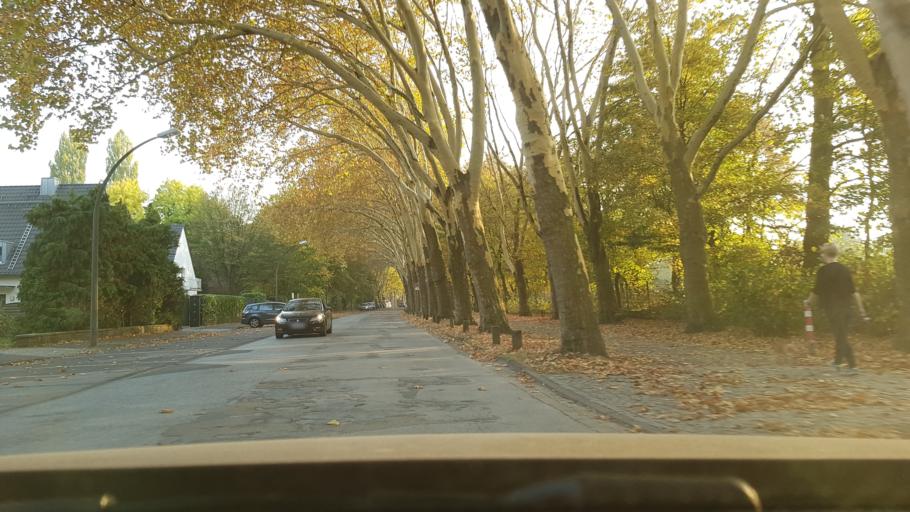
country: DE
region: North Rhine-Westphalia
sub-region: Regierungsbezirk Dusseldorf
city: Hochfeld
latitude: 51.4090
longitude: 6.7074
